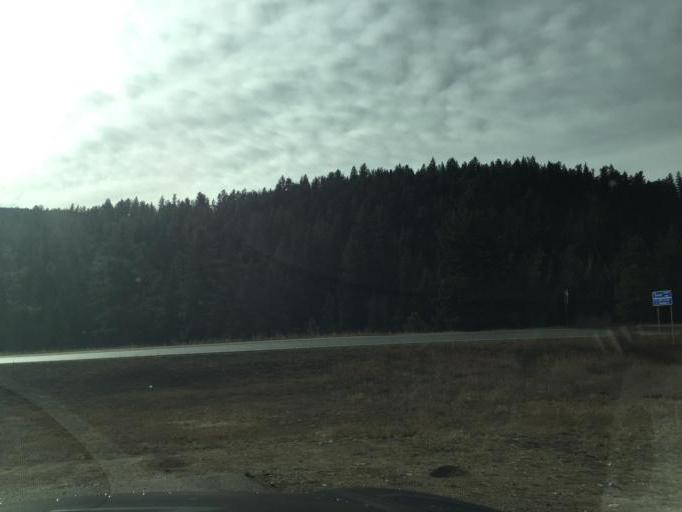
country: US
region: Colorado
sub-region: Jefferson County
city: Evergreen
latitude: 39.4075
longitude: -105.4900
